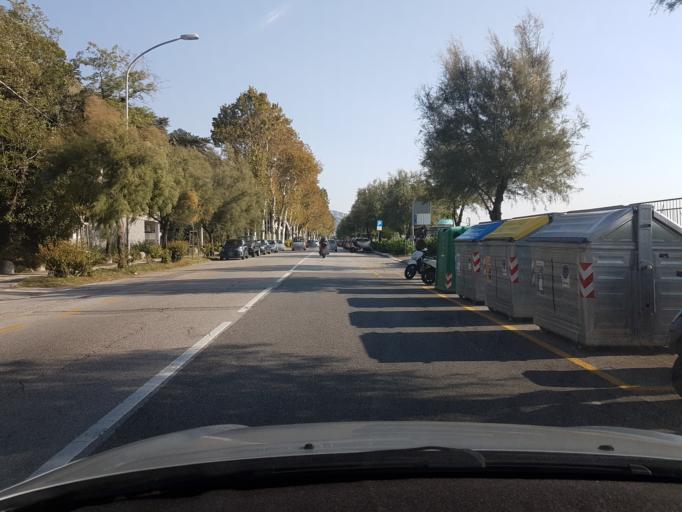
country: IT
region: Friuli Venezia Giulia
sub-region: Provincia di Trieste
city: Prosecco-Contovello
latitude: 45.6938
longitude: 13.7373
